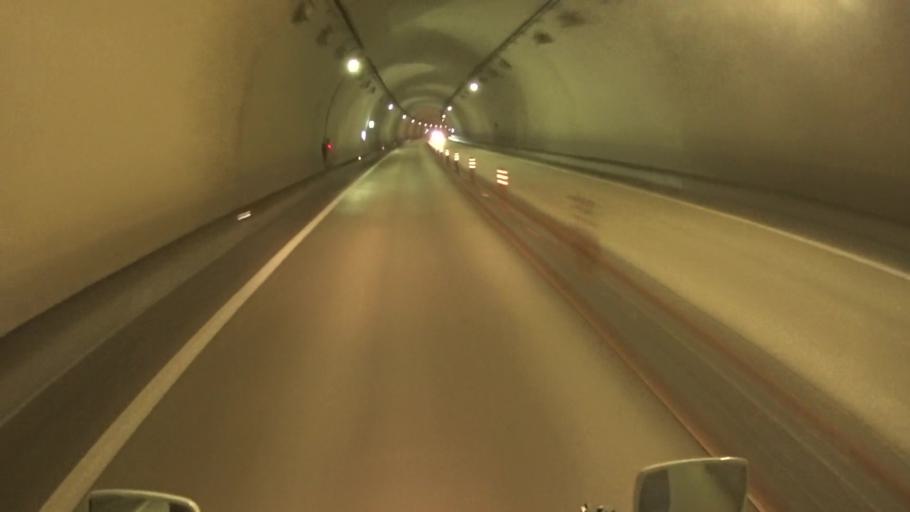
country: JP
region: Kyoto
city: Miyazu
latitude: 35.5464
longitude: 135.1514
